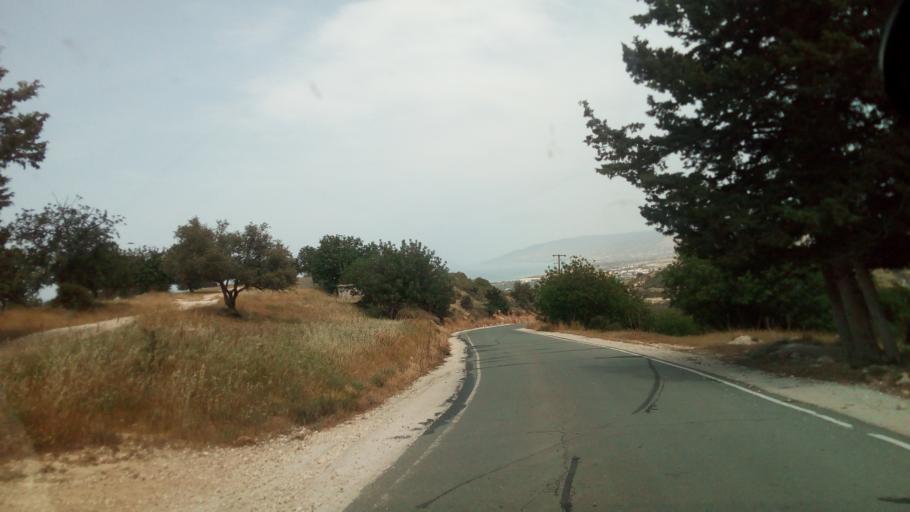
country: CY
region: Pafos
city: Polis
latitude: 35.0126
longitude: 32.3932
